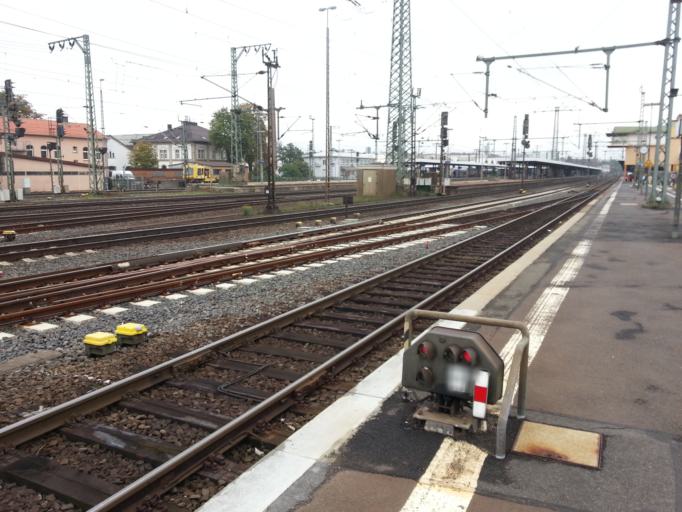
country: DE
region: Hesse
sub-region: Regierungsbezirk Kassel
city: Fulda
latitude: 50.5560
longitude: 9.6822
